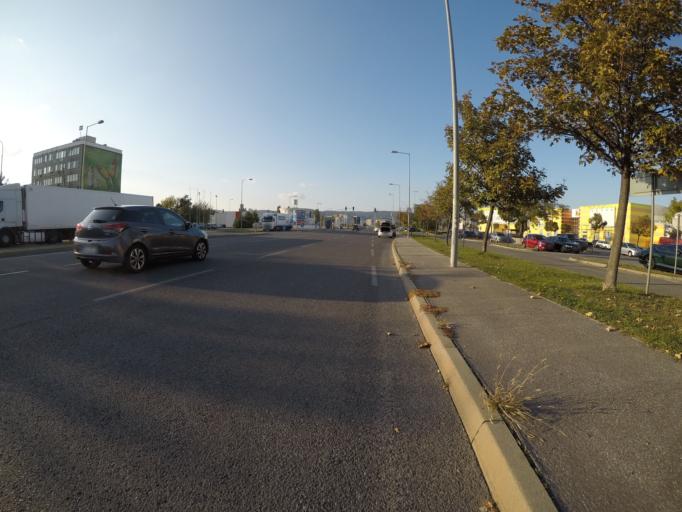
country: SK
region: Bratislavsky
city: Svaty Jur
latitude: 48.1841
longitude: 17.1770
